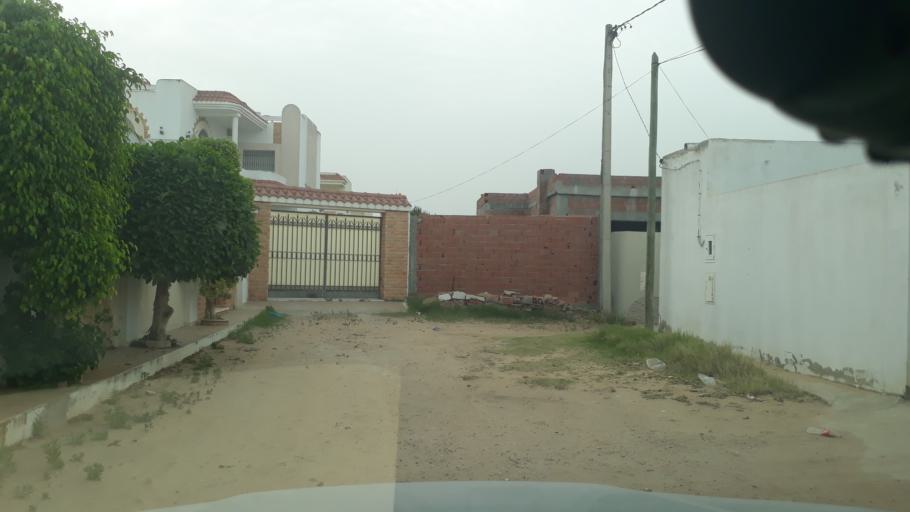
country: TN
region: Safaqis
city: Al Qarmadah
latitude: 34.7838
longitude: 10.7697
